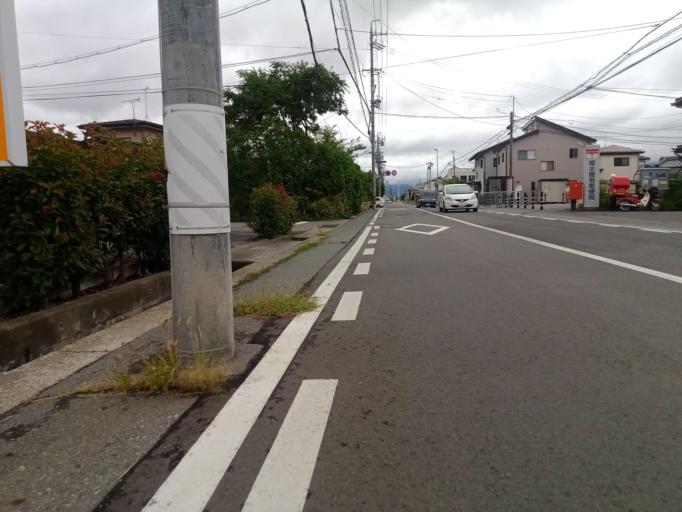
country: JP
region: Nagano
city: Nagano-shi
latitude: 36.6279
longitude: 138.1640
